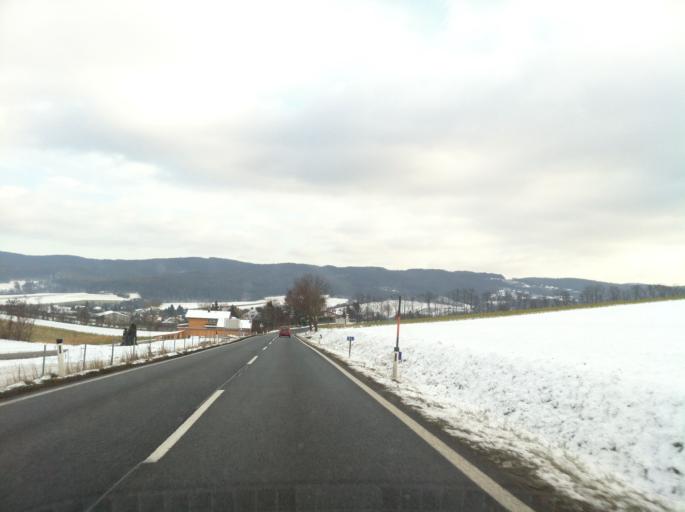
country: AT
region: Lower Austria
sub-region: Politischer Bezirk Tulln
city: Tulln
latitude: 48.2733
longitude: 16.0694
